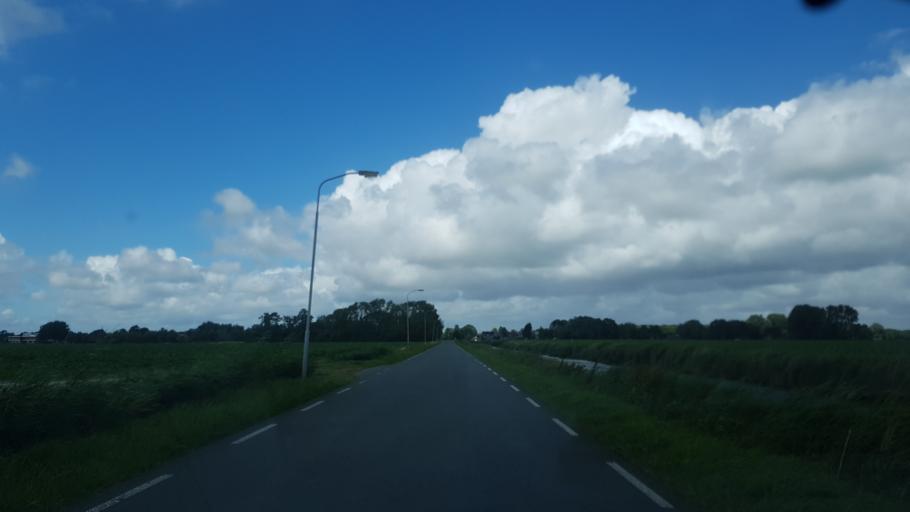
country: NL
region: Groningen
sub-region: Gemeente Bedum
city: Bedum
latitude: 53.3944
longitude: 6.6748
